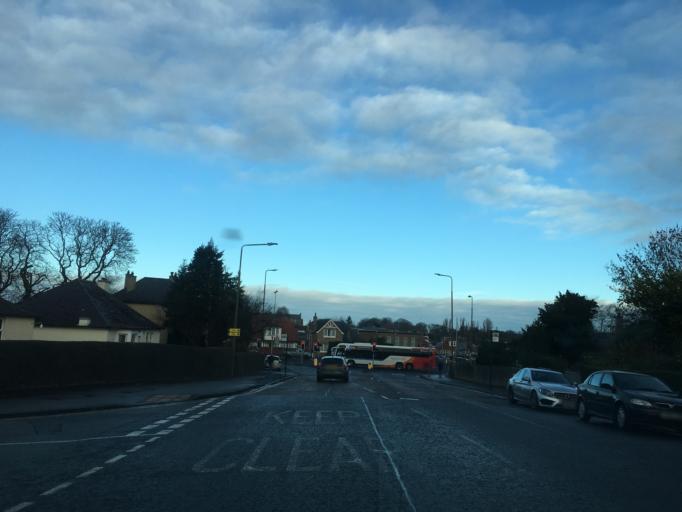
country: GB
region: Scotland
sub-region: Edinburgh
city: Colinton
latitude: 55.9599
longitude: -3.2589
